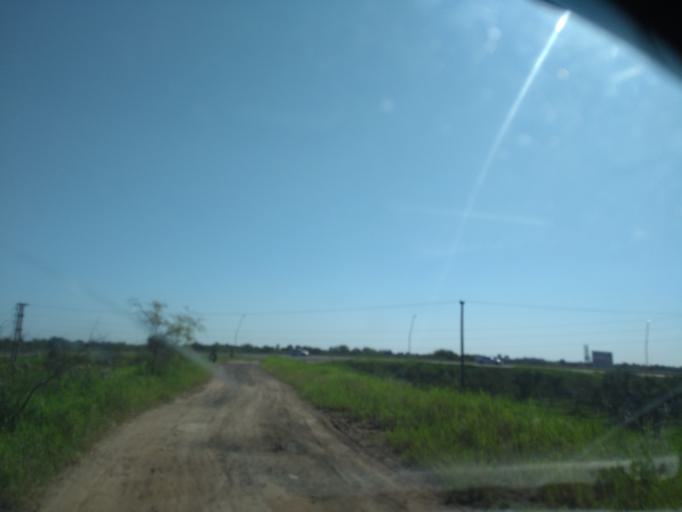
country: AR
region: Chaco
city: Barranqueras
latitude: -27.4418
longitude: -58.8938
